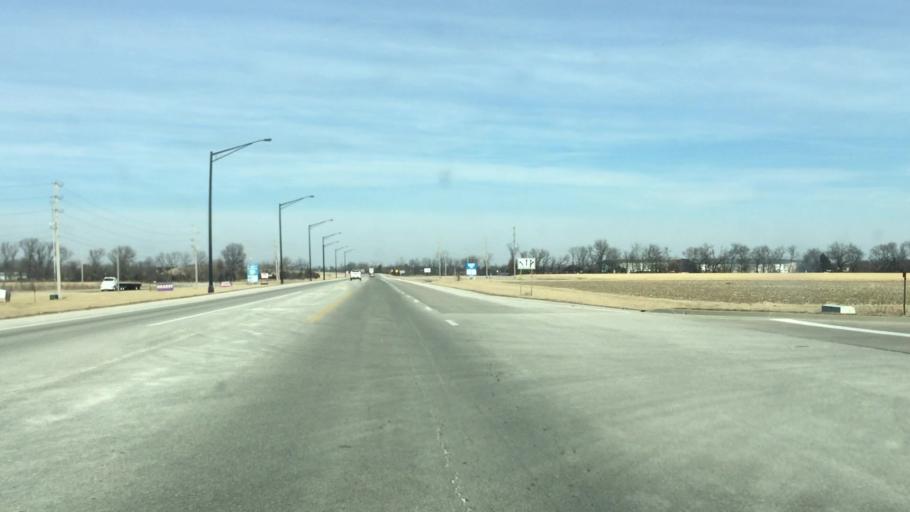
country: US
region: Kansas
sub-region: Labette County
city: Parsons
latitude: 37.3728
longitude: -95.2584
